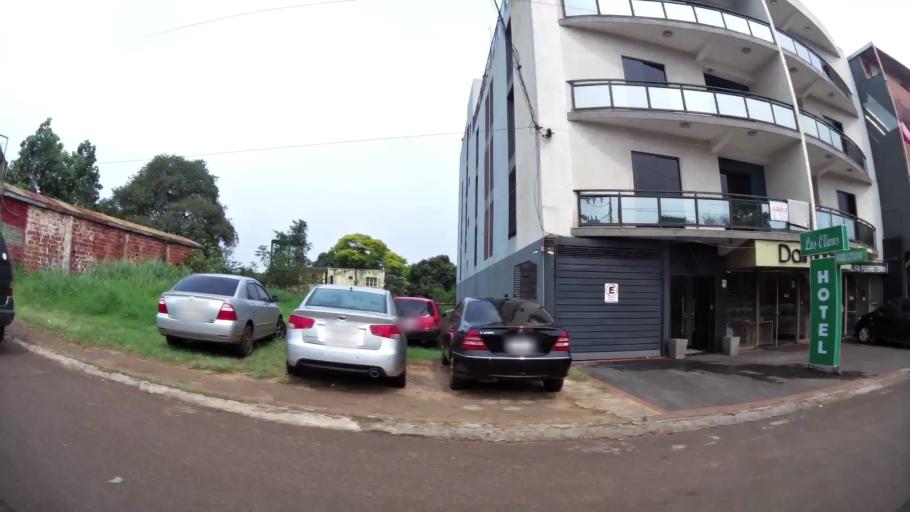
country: PY
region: Alto Parana
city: Presidente Franco
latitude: -25.5382
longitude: -54.6332
